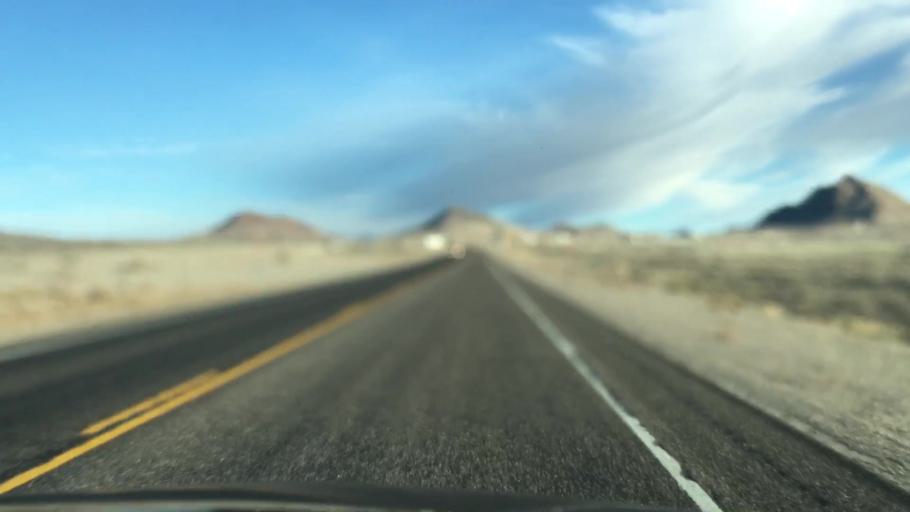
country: US
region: Nevada
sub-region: Nye County
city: Tonopah
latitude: 38.0813
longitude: -117.2670
